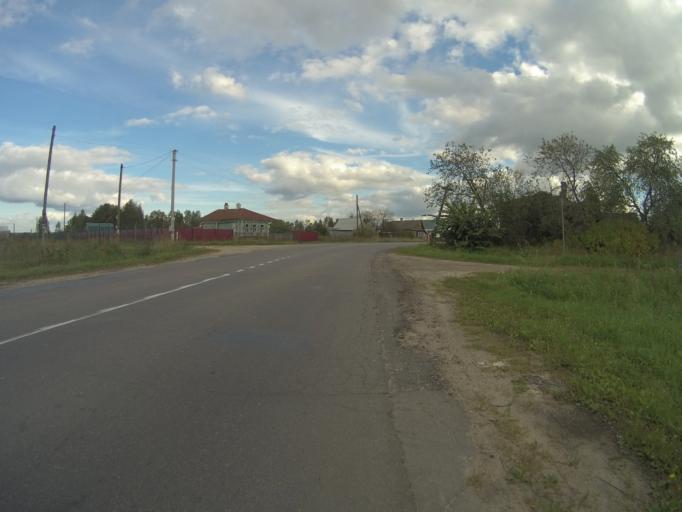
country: RU
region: Vladimir
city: Sudogda
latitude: 56.0390
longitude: 40.8360
